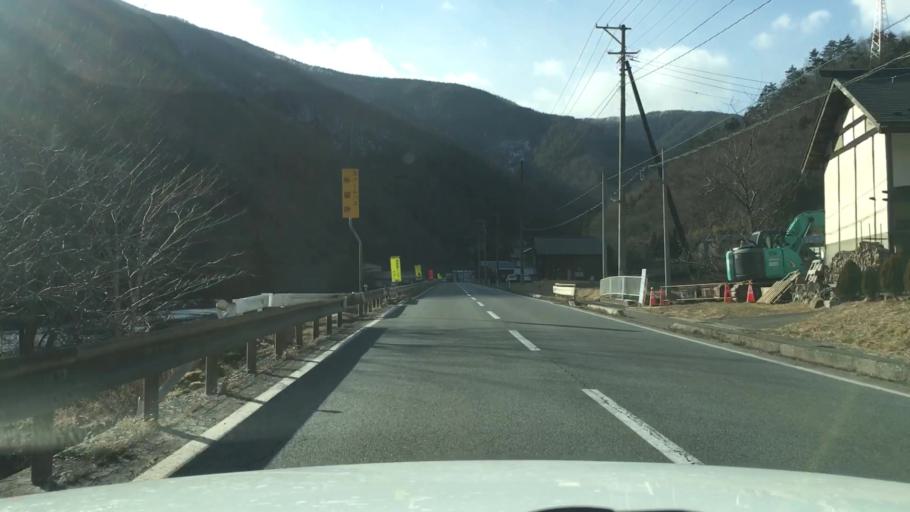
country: JP
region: Iwate
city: Miyako
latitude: 39.6100
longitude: 141.6429
